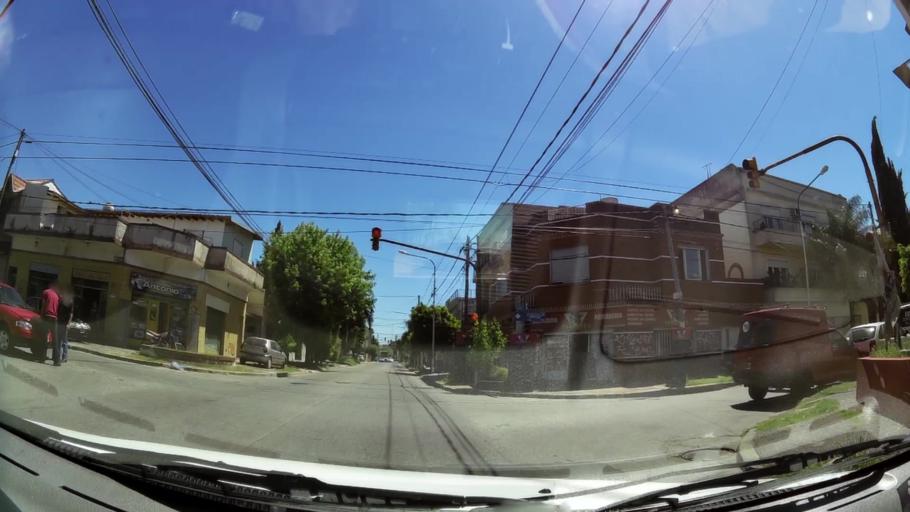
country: AR
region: Buenos Aires
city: Caseros
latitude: -34.5966
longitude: -58.5687
